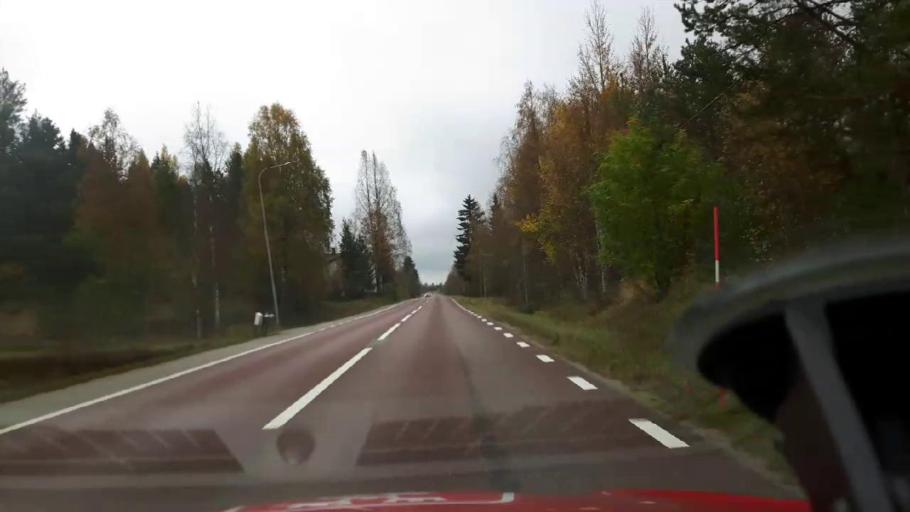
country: SE
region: Jaemtland
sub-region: Harjedalens Kommun
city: Sveg
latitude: 62.2914
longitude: 14.7920
